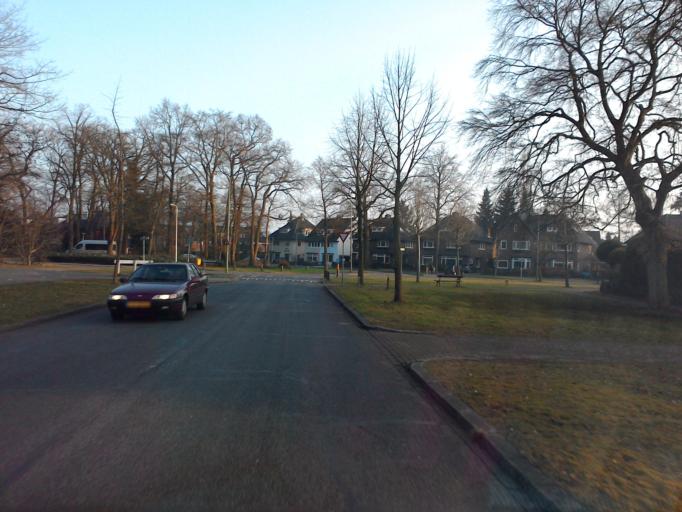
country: NL
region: Utrecht
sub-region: Gemeente Zeist
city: Zeist
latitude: 52.0952
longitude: 5.2268
